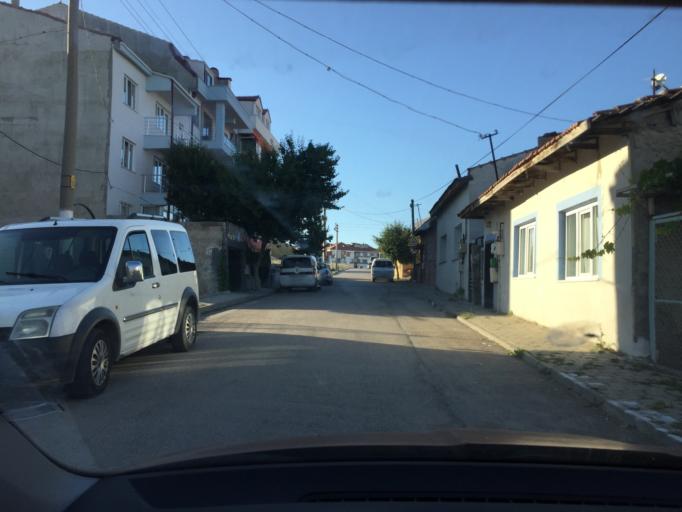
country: TR
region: Eskisehir
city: Eskisehir
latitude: 39.7763
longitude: 30.4529
